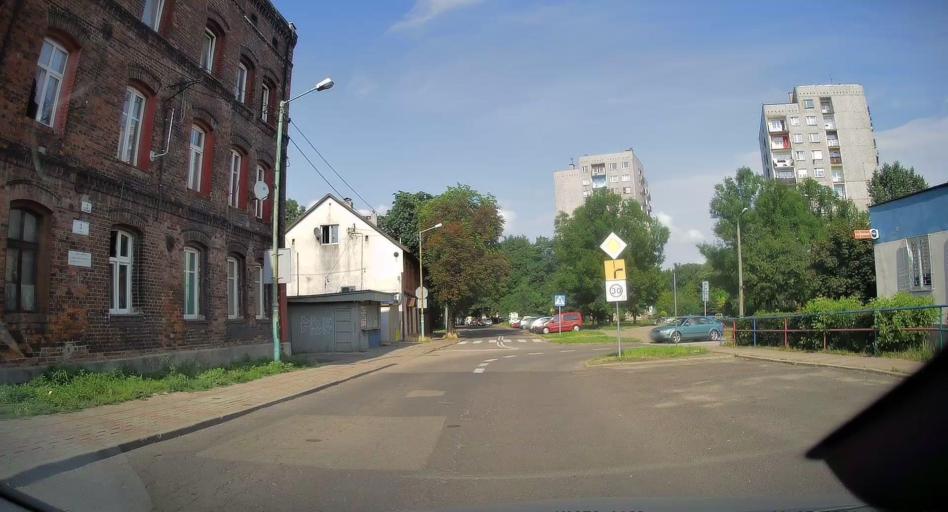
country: PL
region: Silesian Voivodeship
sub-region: Swietochlowice
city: Swietochlowice
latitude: 50.3120
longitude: 18.9155
